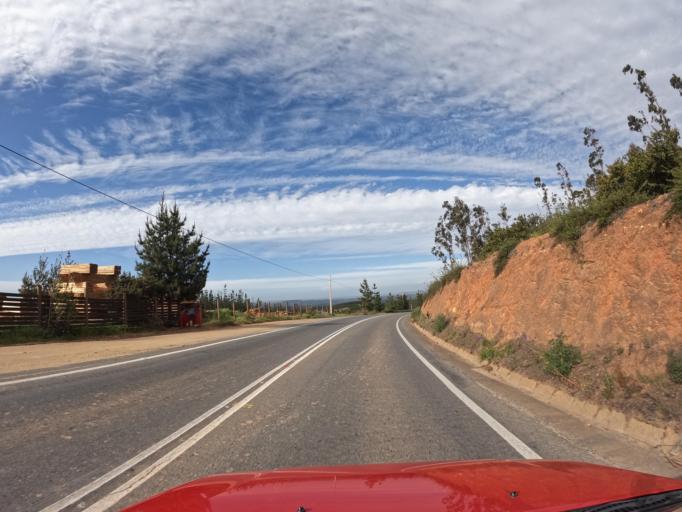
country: CL
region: O'Higgins
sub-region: Provincia de Colchagua
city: Santa Cruz
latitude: -34.3080
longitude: -71.8380
